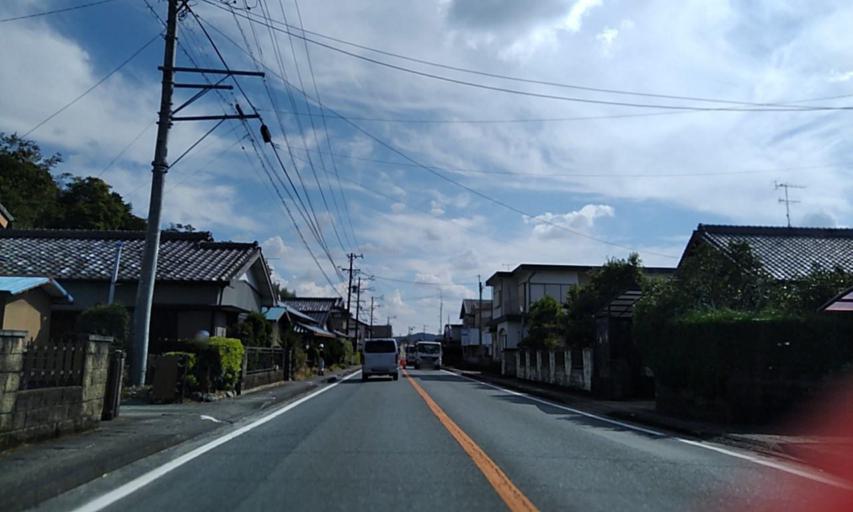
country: JP
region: Shizuoka
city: Hamakita
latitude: 34.8457
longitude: 137.8335
